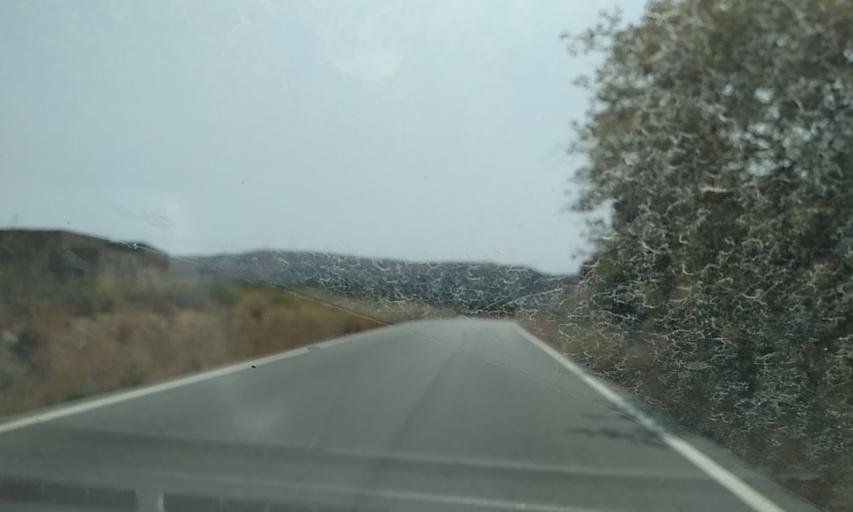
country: GR
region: Crete
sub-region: Nomos Lasithiou
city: Siteia
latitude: 35.1186
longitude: 26.0620
